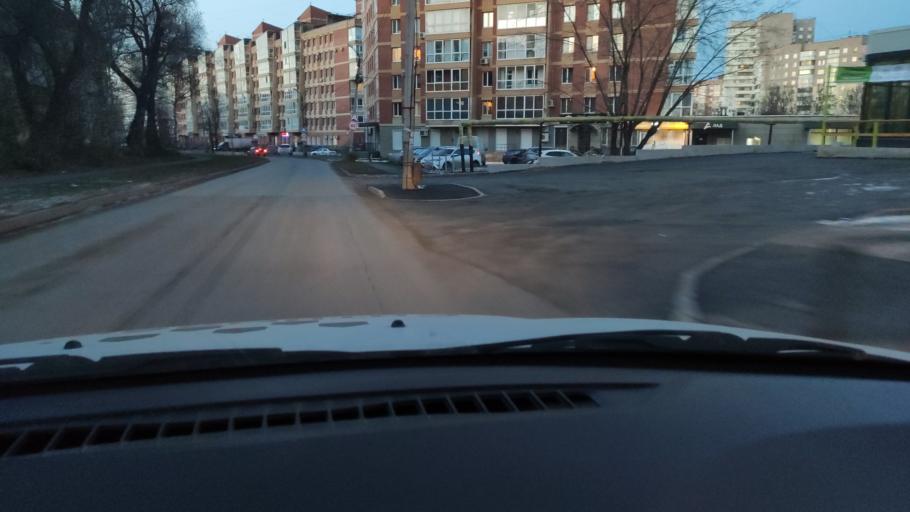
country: RU
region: Perm
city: Perm
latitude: 58.0022
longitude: 56.2952
